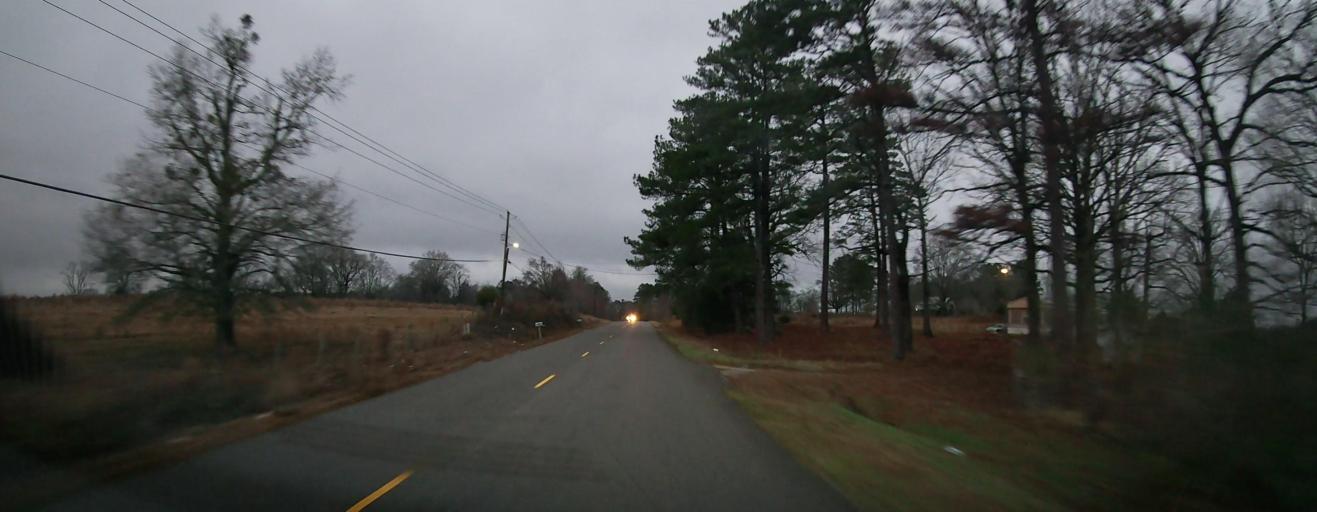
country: US
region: Alabama
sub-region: Tuscaloosa County
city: Vance
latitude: 33.1555
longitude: -87.2299
